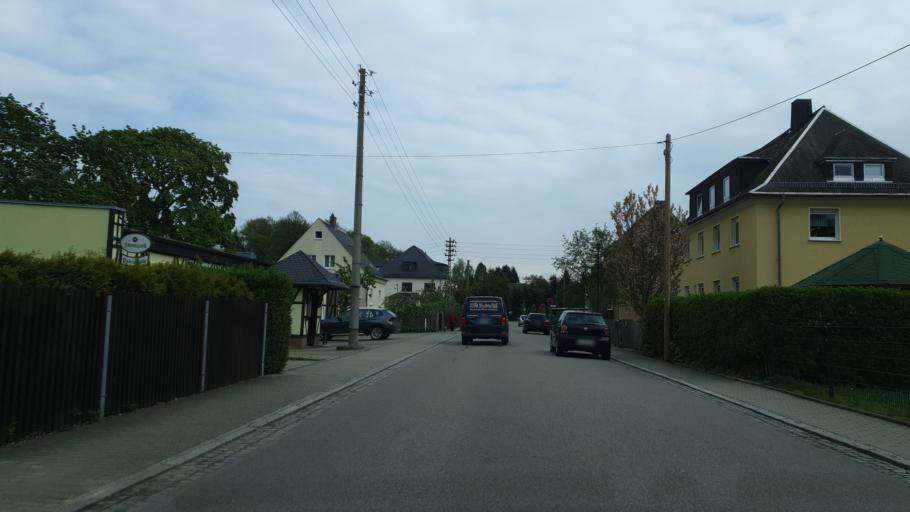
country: DE
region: Saxony
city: Oberlungwitz
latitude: 50.7815
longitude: 12.7093
